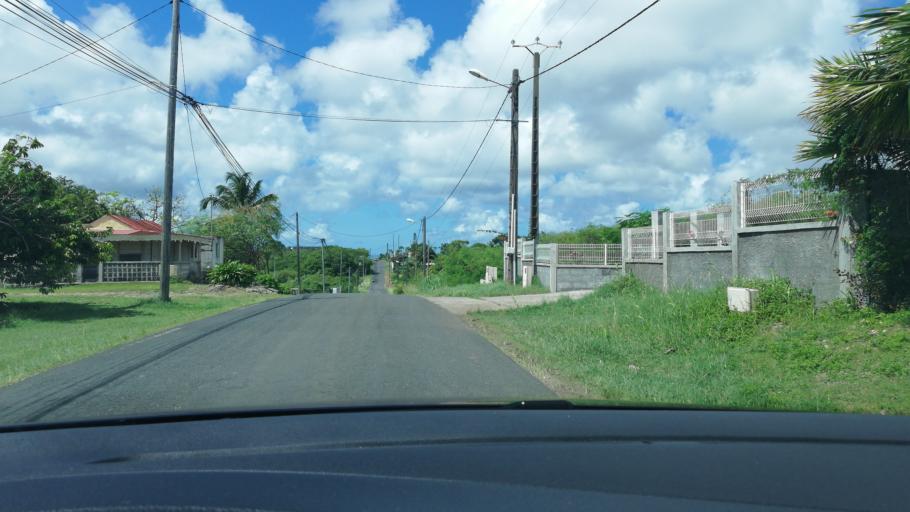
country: GP
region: Guadeloupe
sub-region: Guadeloupe
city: Petit-Canal
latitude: 16.3790
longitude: -61.4441
